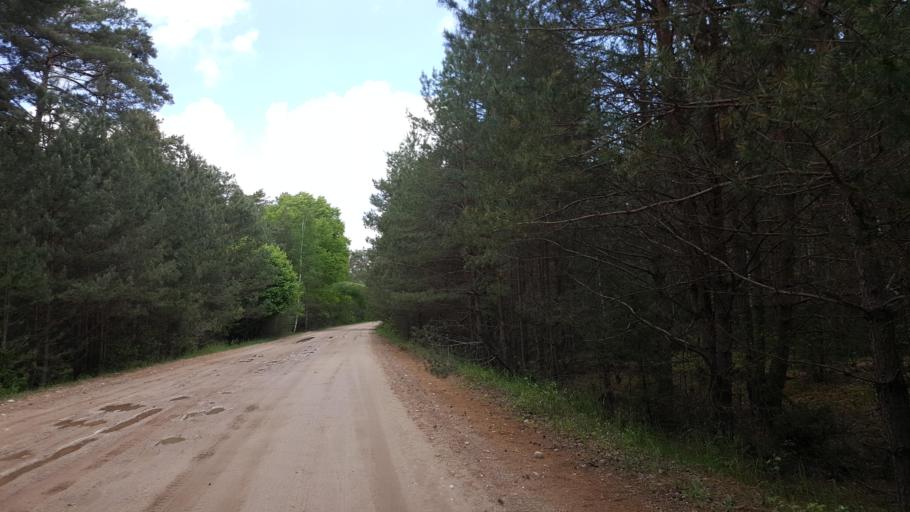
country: BY
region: Brest
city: Kamyanyets
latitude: 52.4614
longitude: 23.9678
